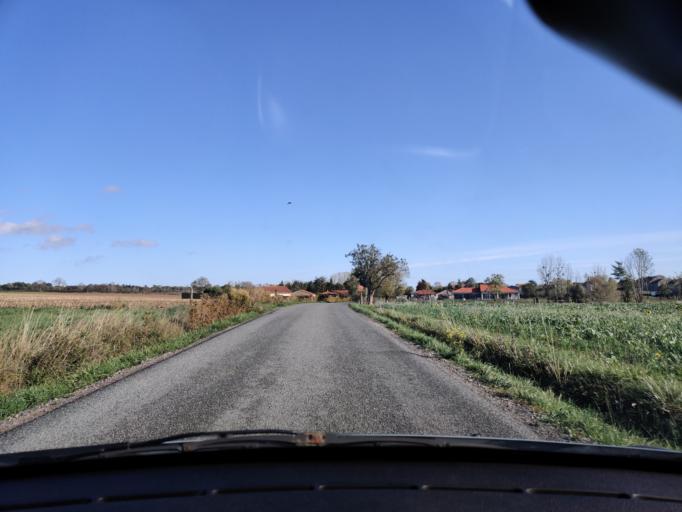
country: FR
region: Auvergne
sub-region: Departement du Puy-de-Dome
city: Combronde
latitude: 46.0354
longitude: 3.1222
